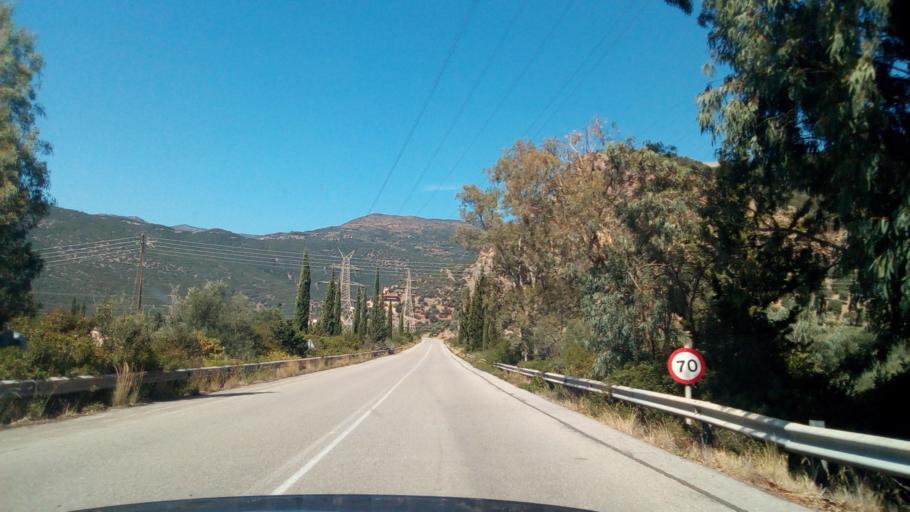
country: GR
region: West Greece
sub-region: Nomos Achaias
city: Aigio
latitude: 38.3647
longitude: 22.1297
